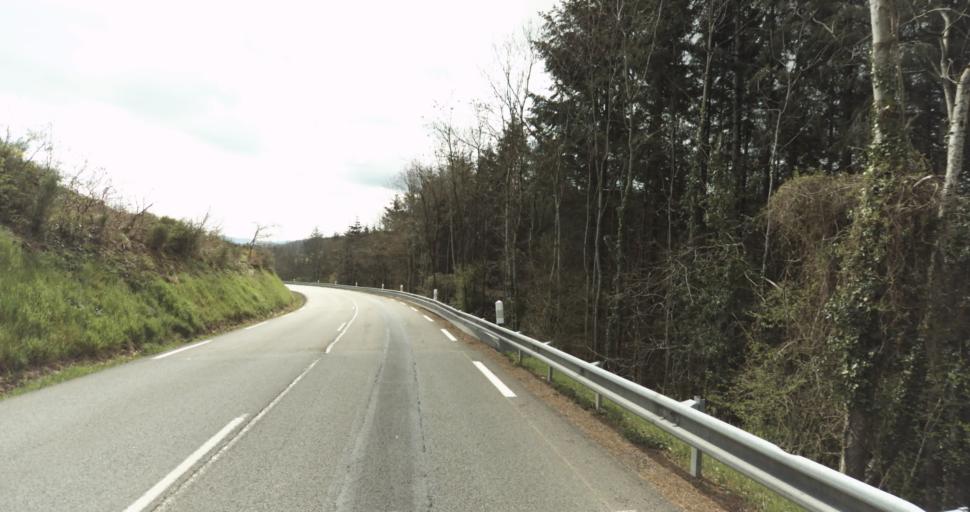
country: FR
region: Rhone-Alpes
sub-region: Departement du Rhone
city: Tarare
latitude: 45.9214
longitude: 4.4067
